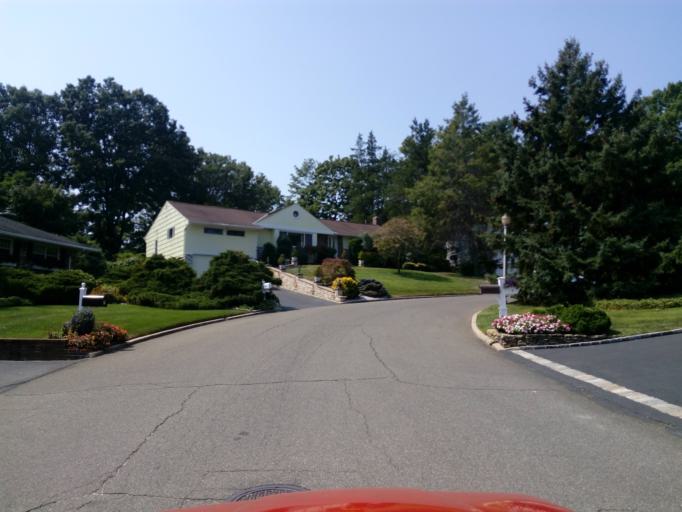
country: US
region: New York
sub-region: Nassau County
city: Glen Cove
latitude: 40.8740
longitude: -73.6364
